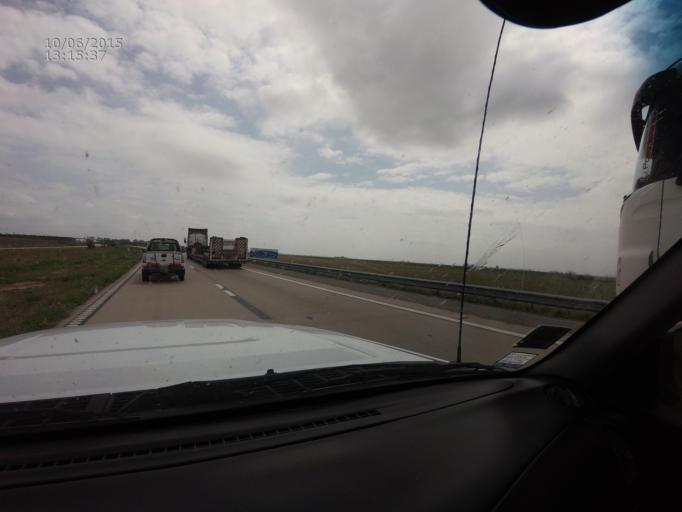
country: AR
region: Cordoba
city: General Roca
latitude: -32.6954
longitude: -61.9559
